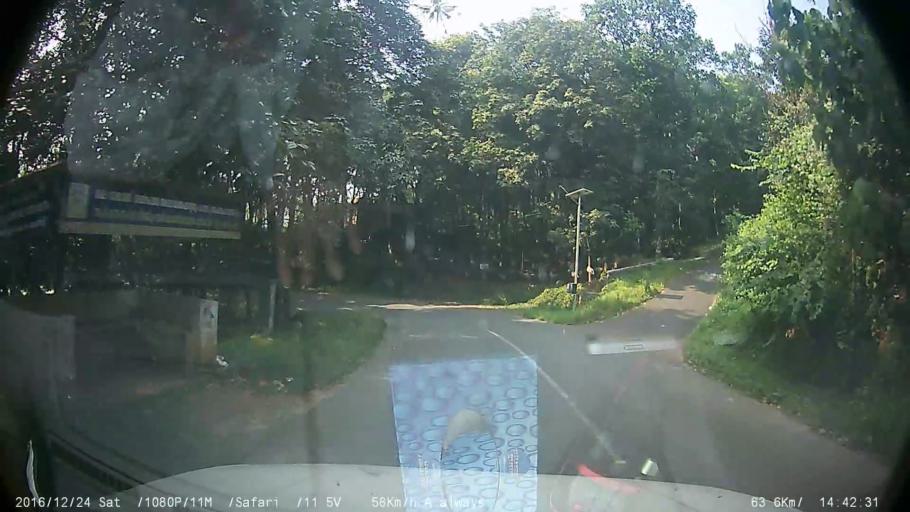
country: IN
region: Kerala
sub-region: Kottayam
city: Lalam
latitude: 9.7803
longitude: 76.7252
